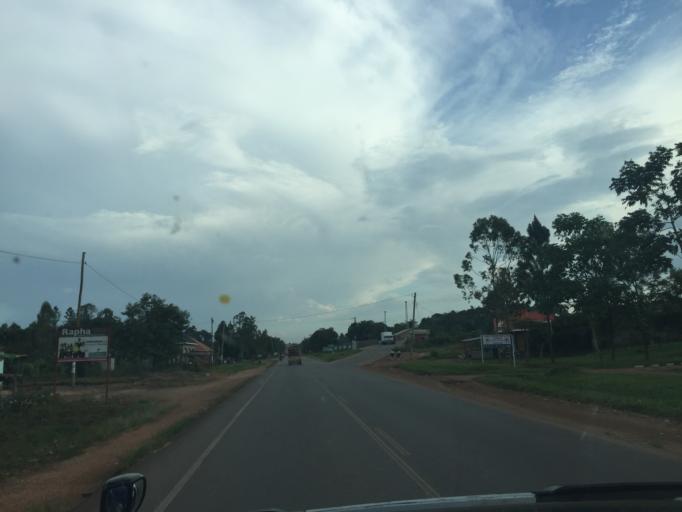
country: UG
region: Central Region
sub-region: Luwero District
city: Luwero
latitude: 0.8639
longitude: 32.4857
